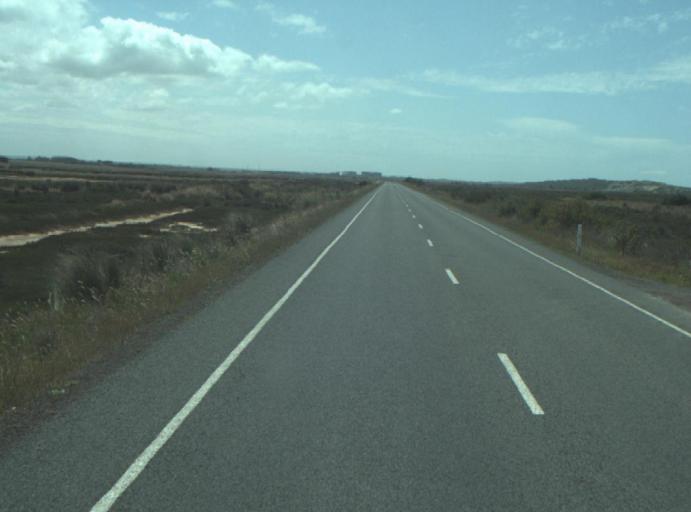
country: AU
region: Victoria
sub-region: Greater Geelong
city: Breakwater
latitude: -38.2905
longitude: 144.3840
